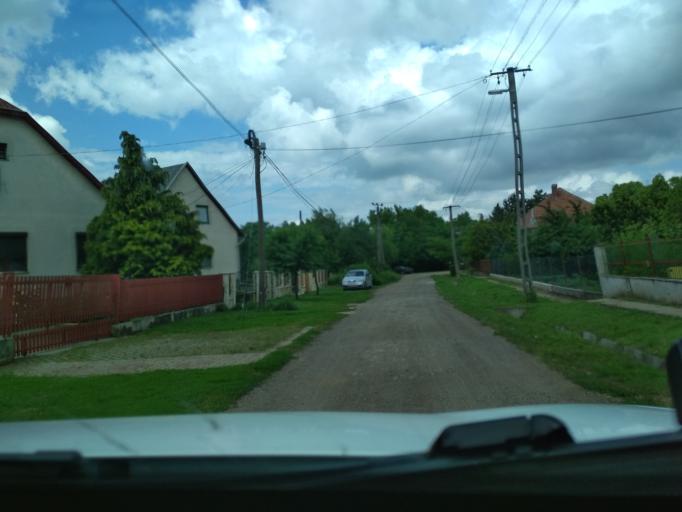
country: HU
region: Jasz-Nagykun-Szolnok
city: Tiszafured
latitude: 47.6117
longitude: 20.7450
